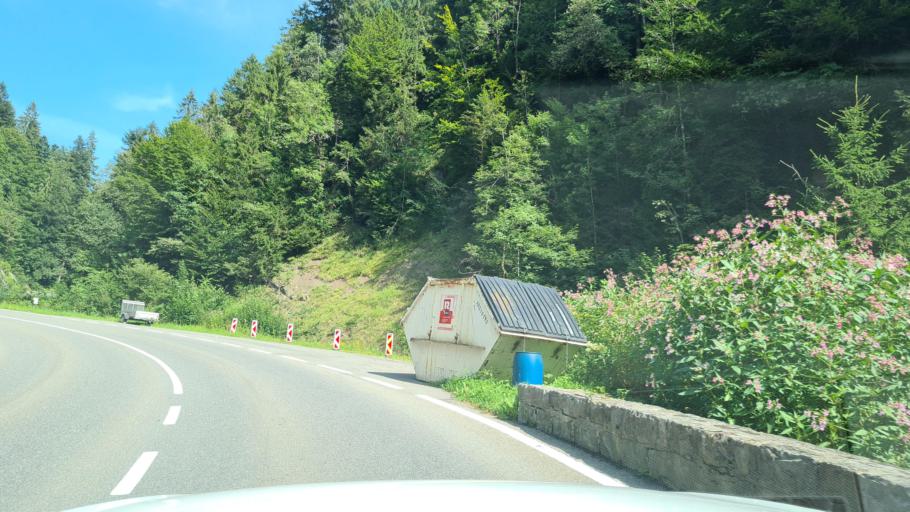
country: AT
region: Vorarlberg
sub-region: Politischer Bezirk Bregenz
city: Bildstein
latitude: 47.4429
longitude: 9.7918
